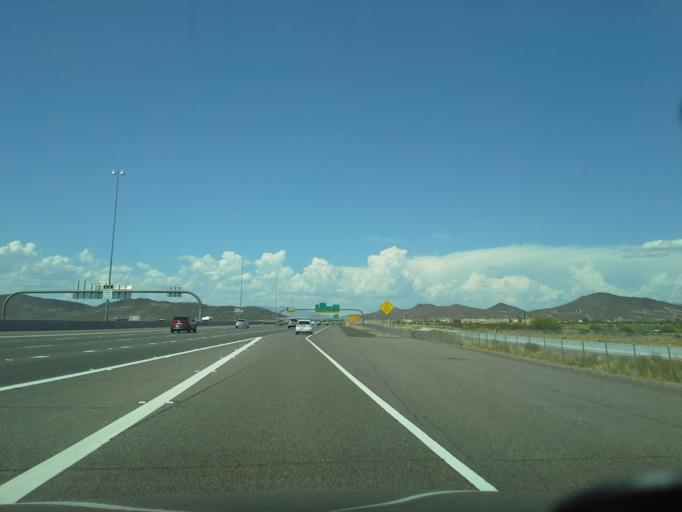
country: US
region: Arizona
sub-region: Maricopa County
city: Anthem
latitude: 33.7887
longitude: -112.1331
